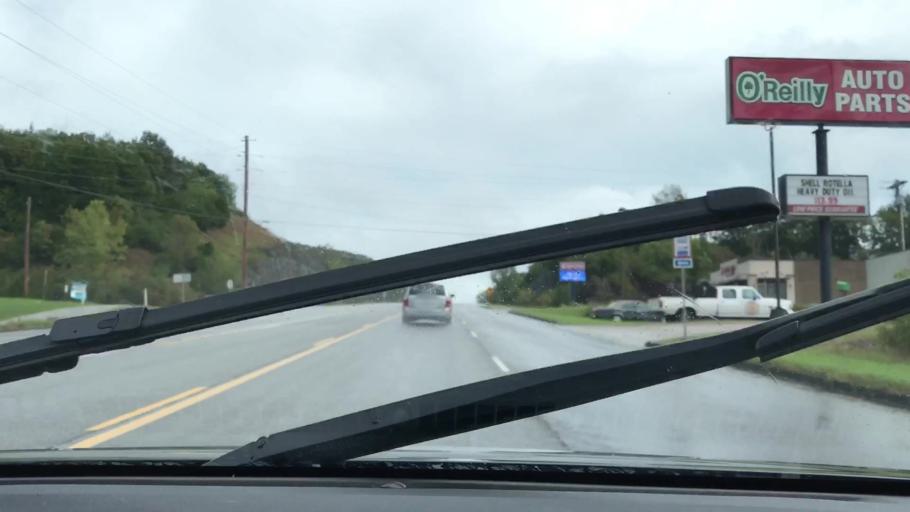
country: US
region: Tennessee
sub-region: Smith County
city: Carthage
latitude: 36.2615
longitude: -85.9492
